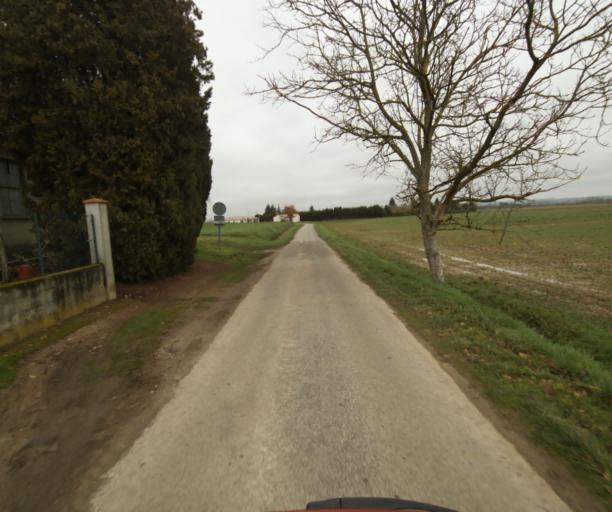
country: FR
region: Midi-Pyrenees
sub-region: Departement de l'Ariege
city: Saverdun
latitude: 43.2573
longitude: 1.5305
